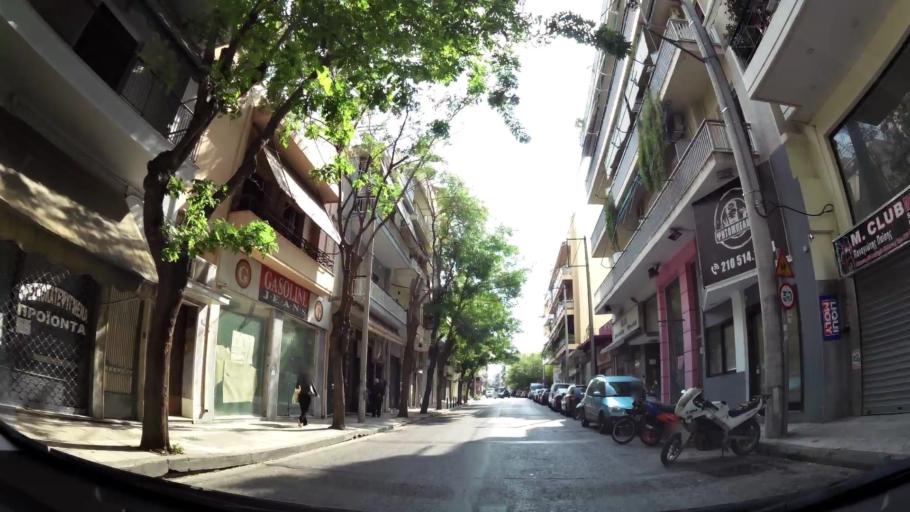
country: GR
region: Attica
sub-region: Nomarchia Athinas
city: Athens
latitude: 37.9885
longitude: 23.7123
